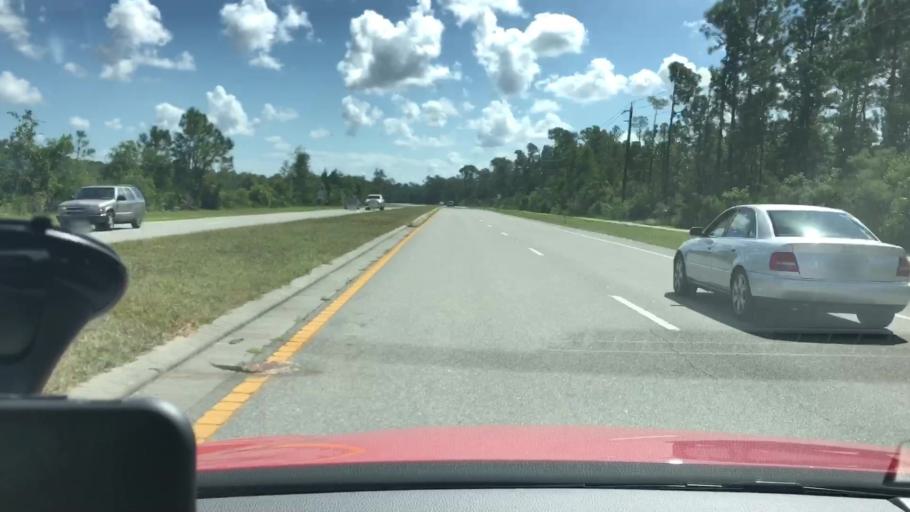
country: US
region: Florida
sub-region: Volusia County
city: Ormond Beach
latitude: 29.2489
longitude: -81.0938
